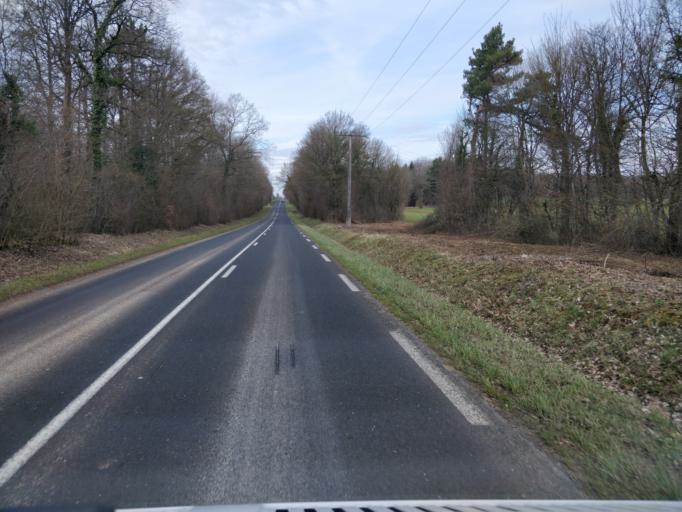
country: FR
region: Lorraine
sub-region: Departement de Meurthe-et-Moselle
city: Montauville
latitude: 48.9193
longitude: 5.9156
